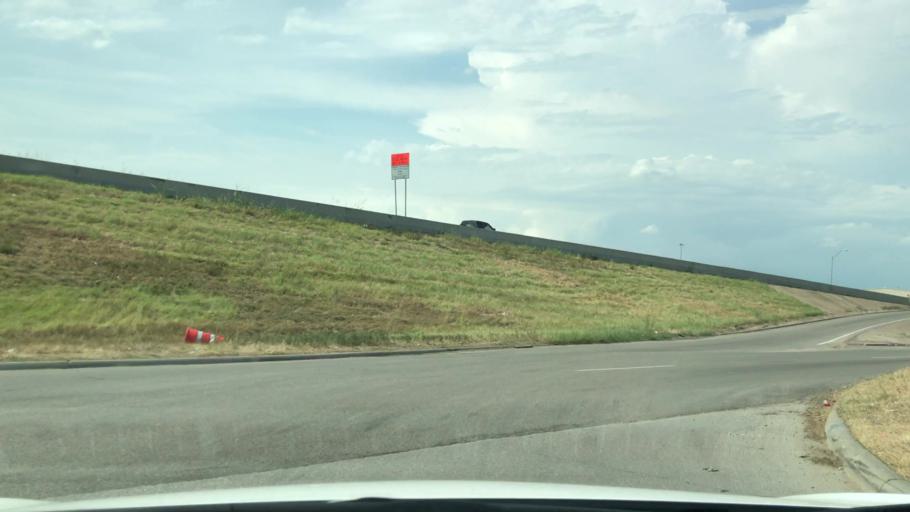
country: US
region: Texas
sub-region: Dallas County
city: Irving
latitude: 32.8309
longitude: -96.9164
